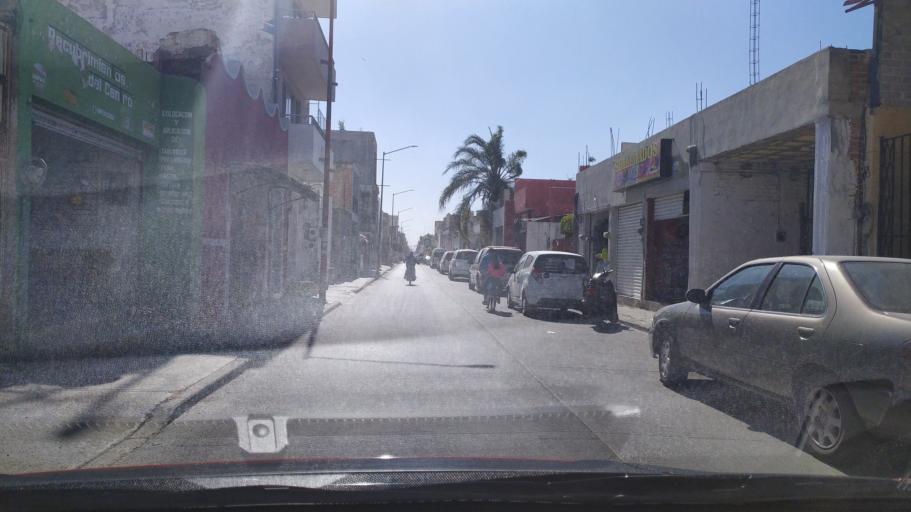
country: MX
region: Guanajuato
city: San Francisco del Rincon
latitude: 21.0230
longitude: -101.8582
